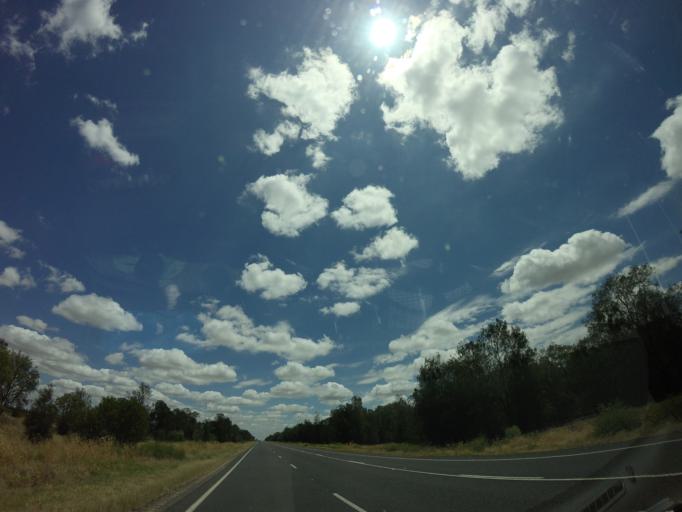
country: AU
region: New South Wales
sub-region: Moree Plains
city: Boggabilla
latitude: -28.9748
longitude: 150.0802
